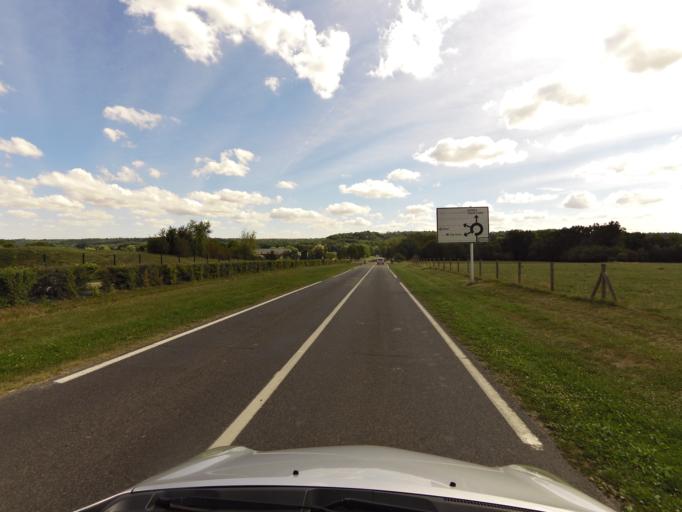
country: FR
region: Picardie
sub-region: Departement de l'Aisne
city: Bruyeres-et-Montberault
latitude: 49.4707
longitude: 3.6648
